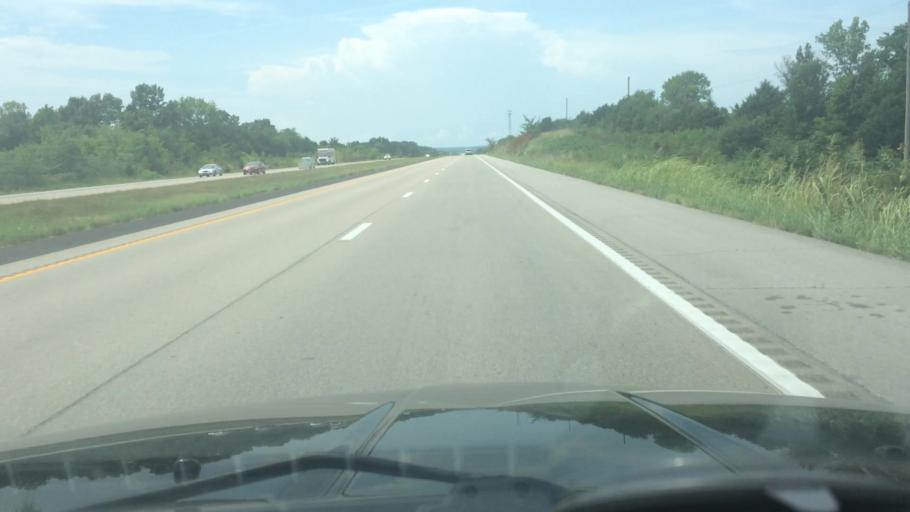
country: US
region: Missouri
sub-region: Polk County
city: Humansville
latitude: 37.7725
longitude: -93.5674
